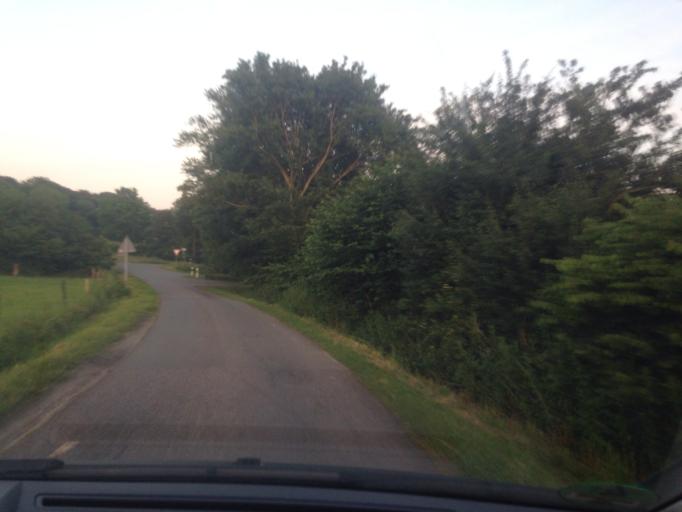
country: DE
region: North Rhine-Westphalia
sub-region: Regierungsbezirk Munster
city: Greven
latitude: 52.0171
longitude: 7.5580
